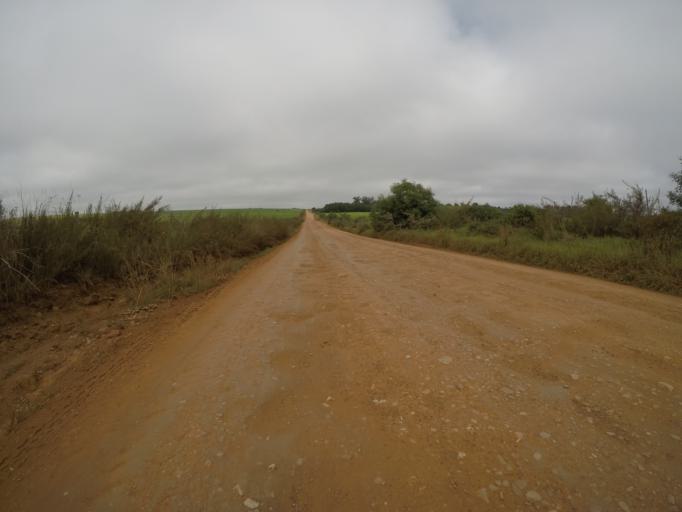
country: ZA
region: Eastern Cape
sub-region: Cacadu District Municipality
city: Kareedouw
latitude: -34.0110
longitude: 24.2369
